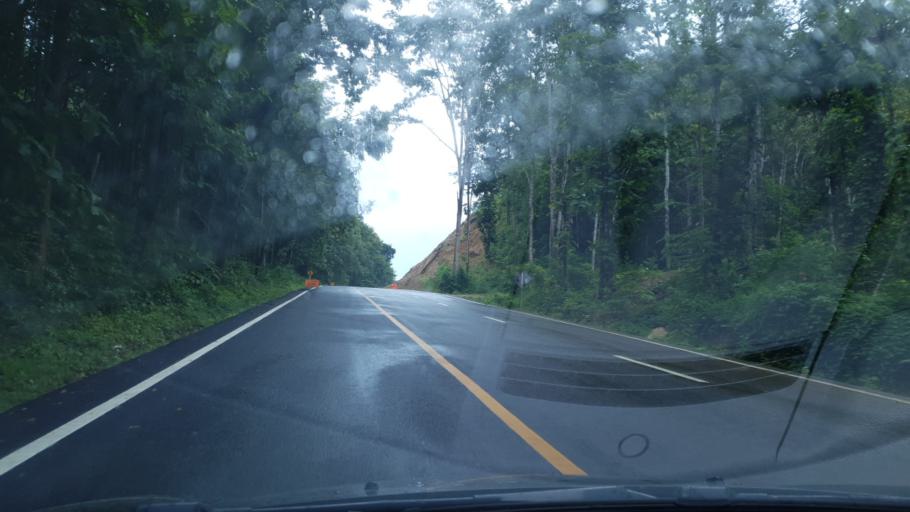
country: TH
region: Mae Hong Son
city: Pa Pae
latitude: 18.2667
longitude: 97.9427
